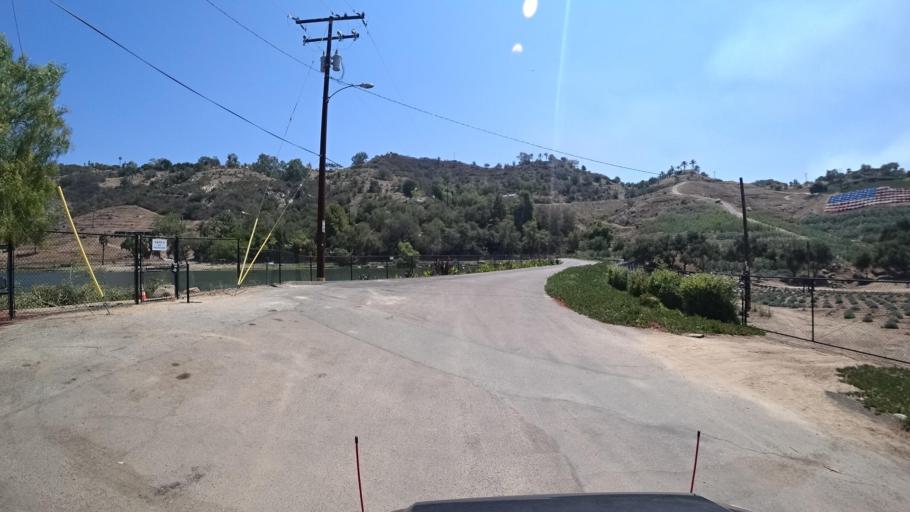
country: US
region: California
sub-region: San Diego County
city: Fallbrook
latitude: 33.4399
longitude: -117.2871
